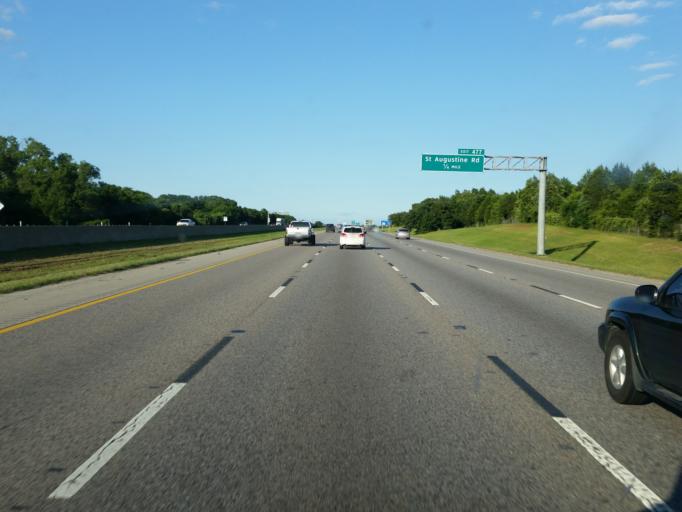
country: US
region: Texas
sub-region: Dallas County
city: Hutchins
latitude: 32.6801
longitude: -96.6697
